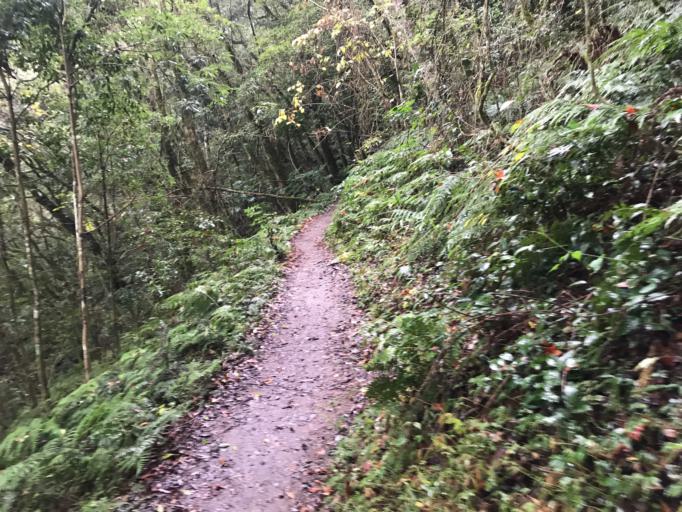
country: TW
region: Taiwan
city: Daxi
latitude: 24.5494
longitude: 121.2920
